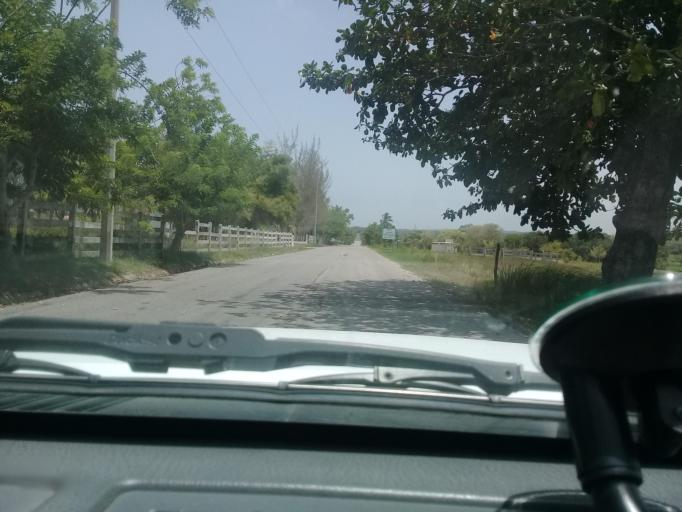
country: MX
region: Veracruz
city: Villa Cuauhtemoc
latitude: 22.1475
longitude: -97.7949
